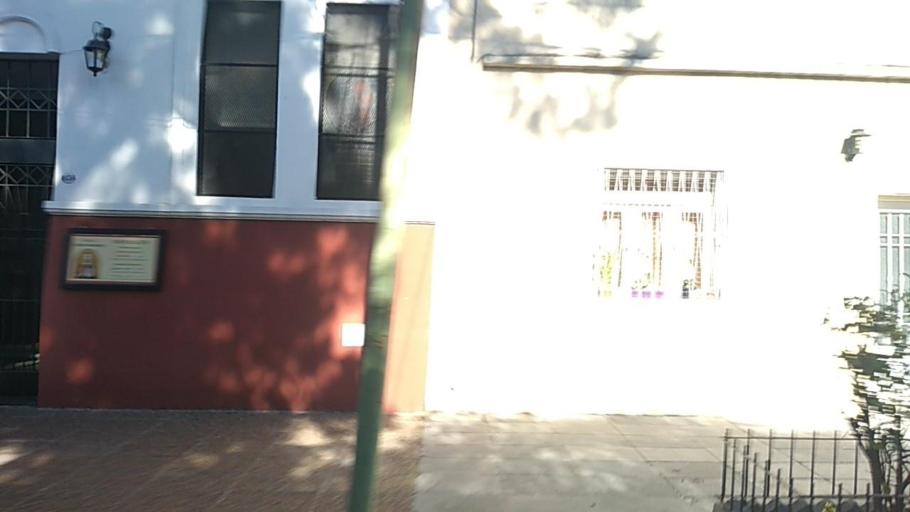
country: AR
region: Buenos Aires F.D.
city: Villa Santa Rita
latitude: -34.6197
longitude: -58.4947
